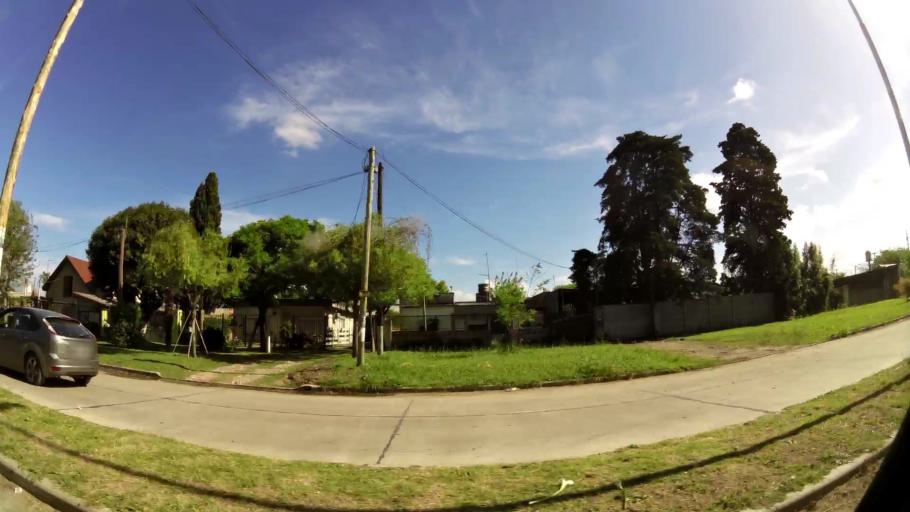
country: AR
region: Buenos Aires
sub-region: Partido de Quilmes
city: Quilmes
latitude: -34.8079
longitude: -58.2187
